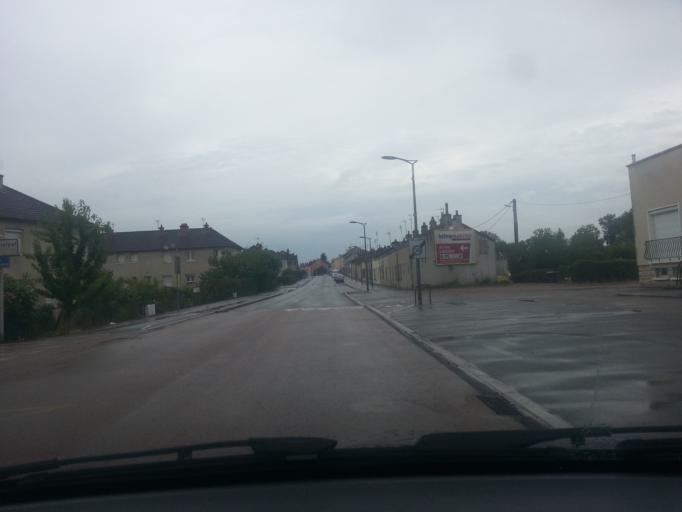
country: FR
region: Bourgogne
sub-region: Departement de Saone-et-Loire
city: Montchanin
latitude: 46.7540
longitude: 4.4747
